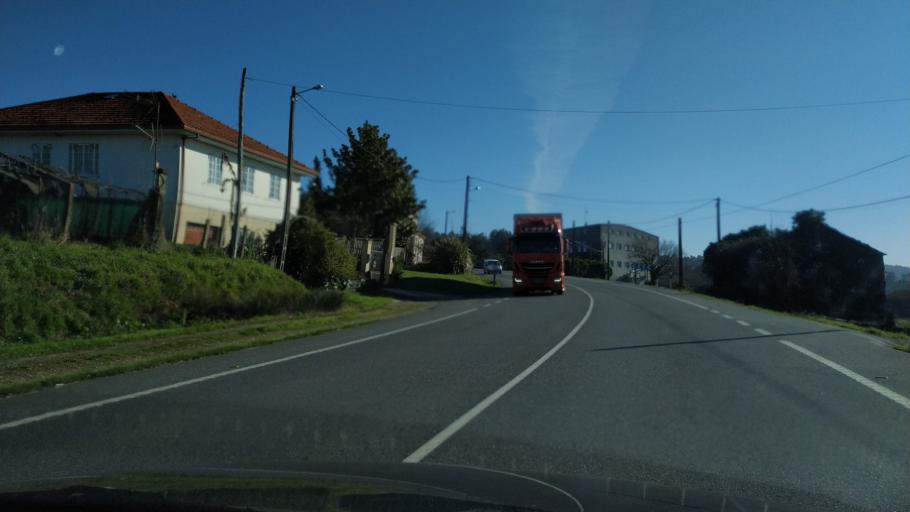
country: ES
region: Galicia
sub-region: Provincia da Coruna
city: Ribeira
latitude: 42.7531
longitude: -8.3848
